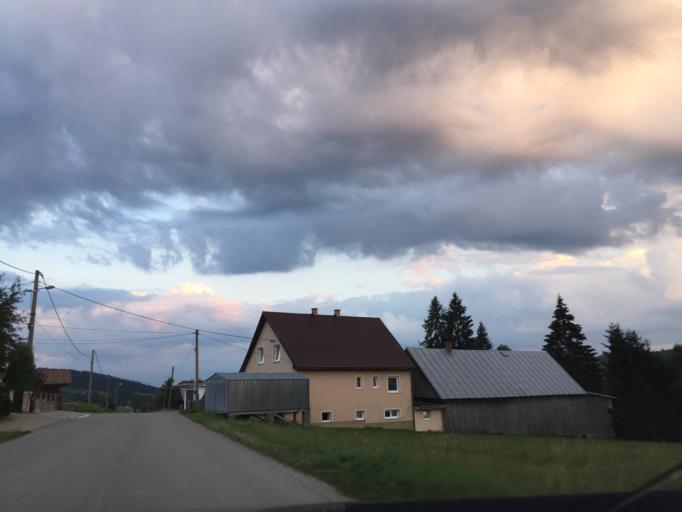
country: PL
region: Silesian Voivodeship
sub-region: Powiat zywiecki
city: Sopotnia Wielka
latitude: 49.4629
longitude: 19.3002
